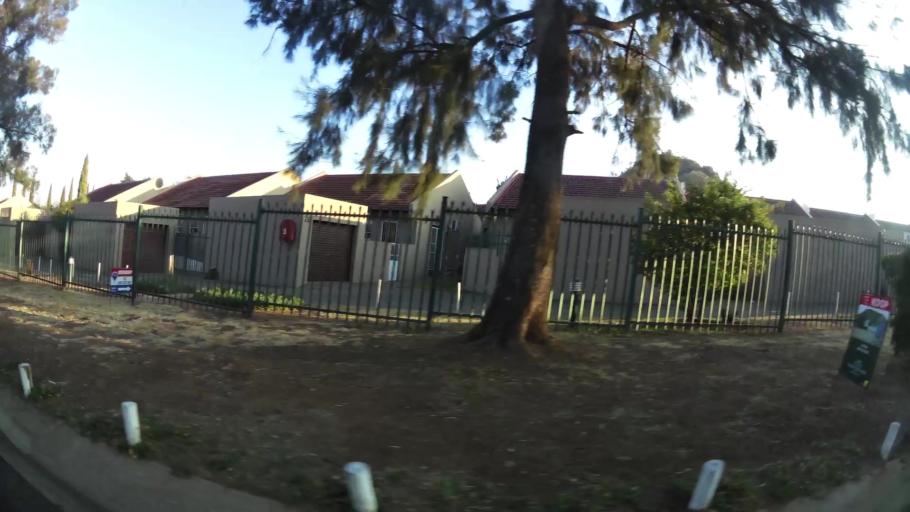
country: ZA
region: Orange Free State
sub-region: Mangaung Metropolitan Municipality
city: Bloemfontein
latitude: -29.0957
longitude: 26.1566
